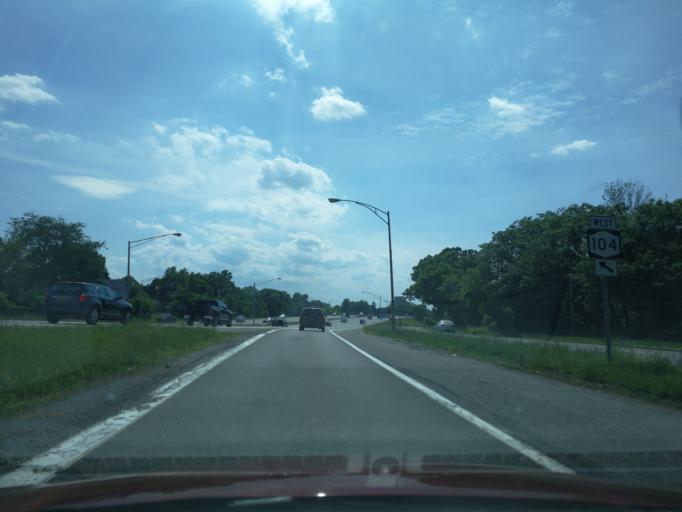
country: US
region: New York
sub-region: Monroe County
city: Irondequoit
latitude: 43.1932
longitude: -77.5946
